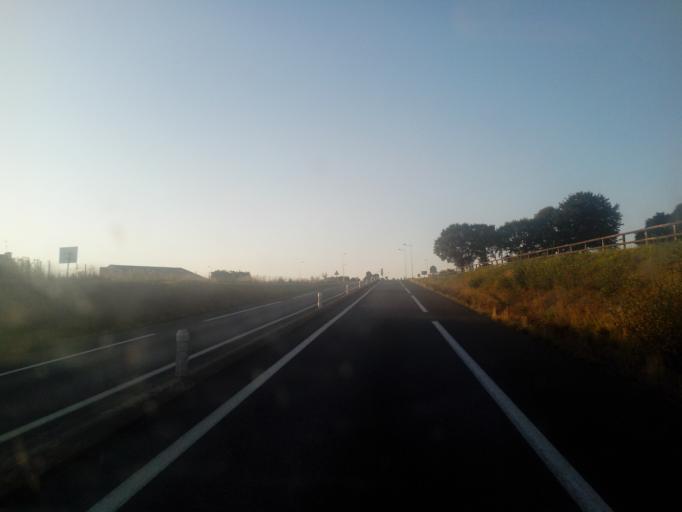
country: FR
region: Brittany
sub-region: Departement des Cotes-d'Armor
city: Loudeac
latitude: 48.1956
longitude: -2.7518
